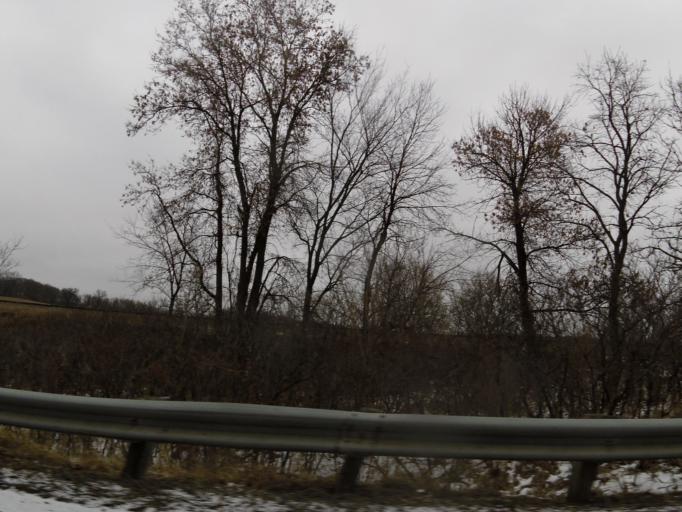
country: US
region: Minnesota
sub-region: Hennepin County
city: Independence
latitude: 45.0180
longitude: -93.7017
